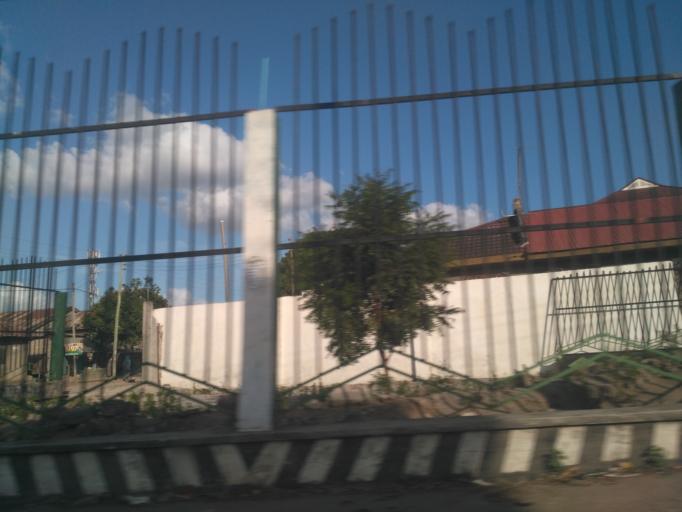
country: TZ
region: Dar es Salaam
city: Dar es Salaam
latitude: -6.8501
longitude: 39.2582
